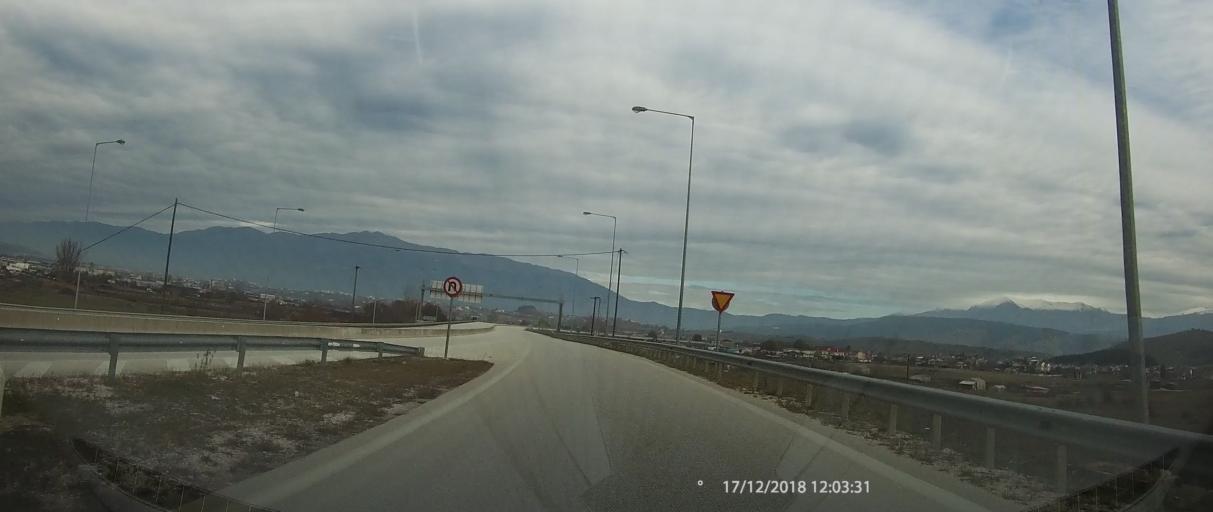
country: GR
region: Epirus
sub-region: Nomos Ioanninon
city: Pedini
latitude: 39.5973
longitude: 20.8645
